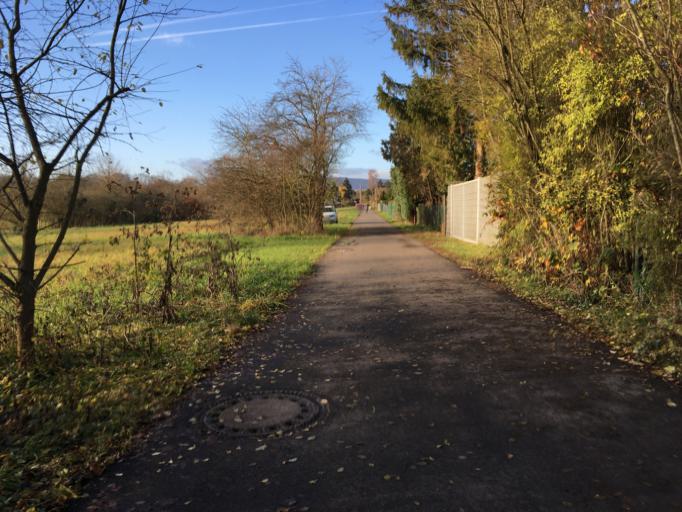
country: DE
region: Hesse
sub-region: Regierungsbezirk Darmstadt
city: Wiesbaden
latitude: 50.0575
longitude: 8.2310
